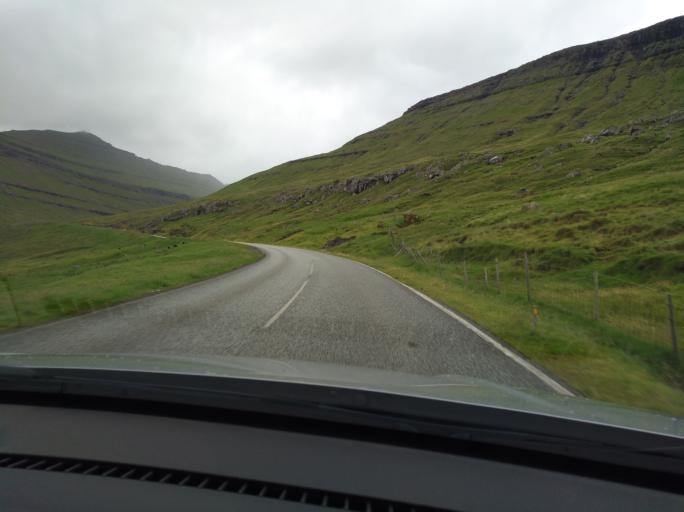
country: FO
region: Eysturoy
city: Fuglafjordur
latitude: 62.2162
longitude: -6.8637
